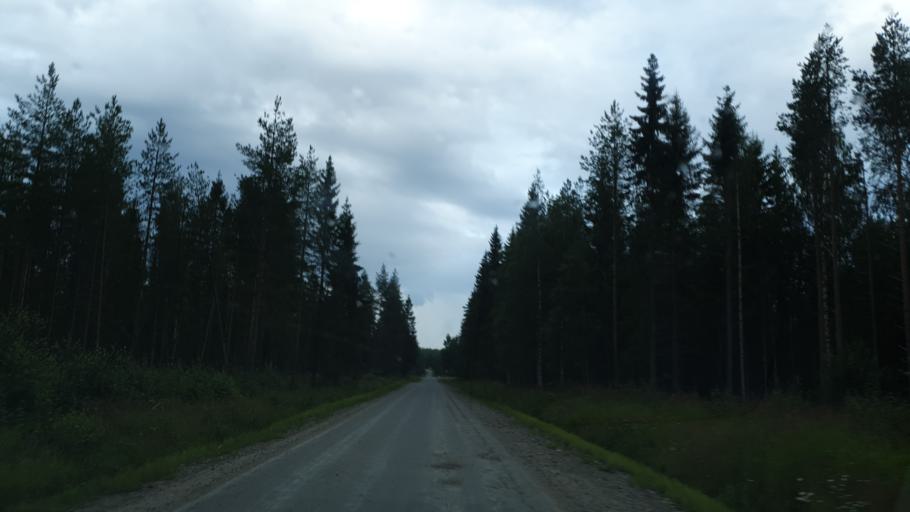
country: FI
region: Kainuu
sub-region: Kehys-Kainuu
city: Kuhmo
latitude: 64.2137
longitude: 29.3687
